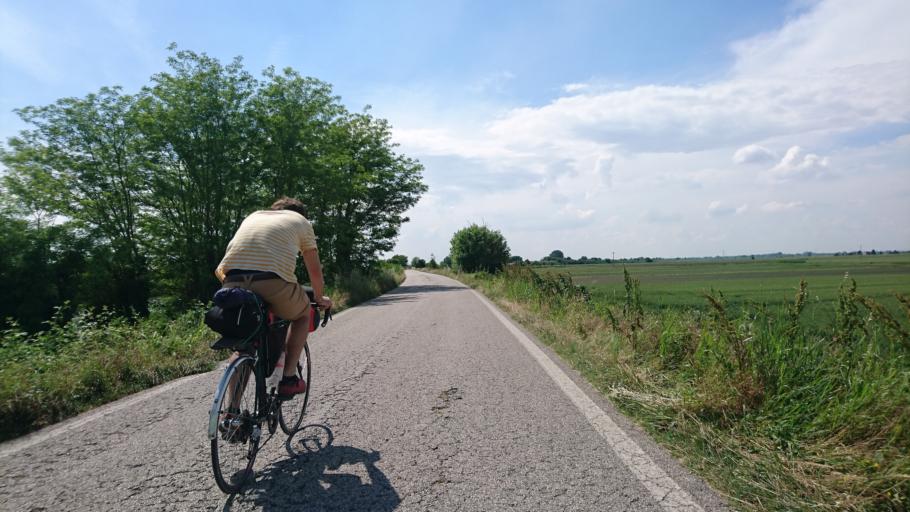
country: IT
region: Veneto
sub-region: Provincia di Rovigo
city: Ceneselli
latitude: 45.0727
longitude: 11.3498
